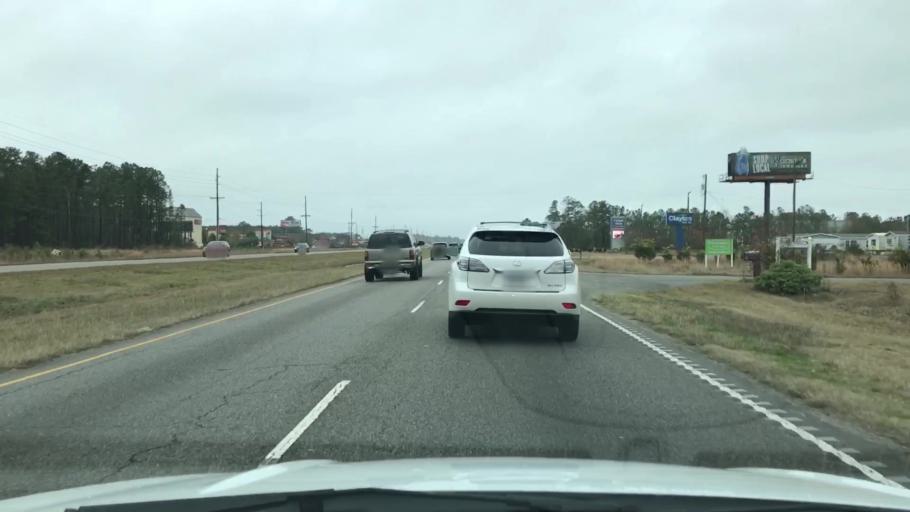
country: US
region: South Carolina
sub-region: Horry County
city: Red Hill
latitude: 33.7848
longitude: -78.9914
